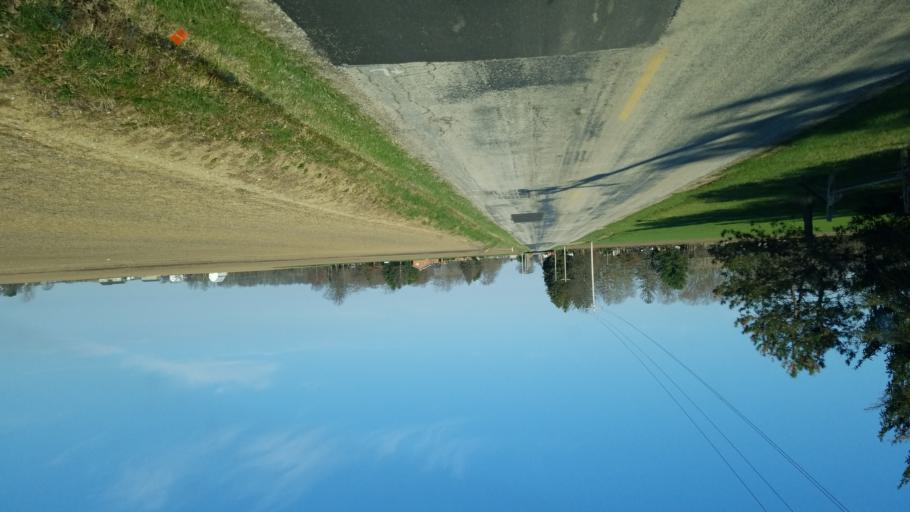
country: US
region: Ohio
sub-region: Morrow County
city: Cardington
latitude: 40.4991
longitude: -82.9868
